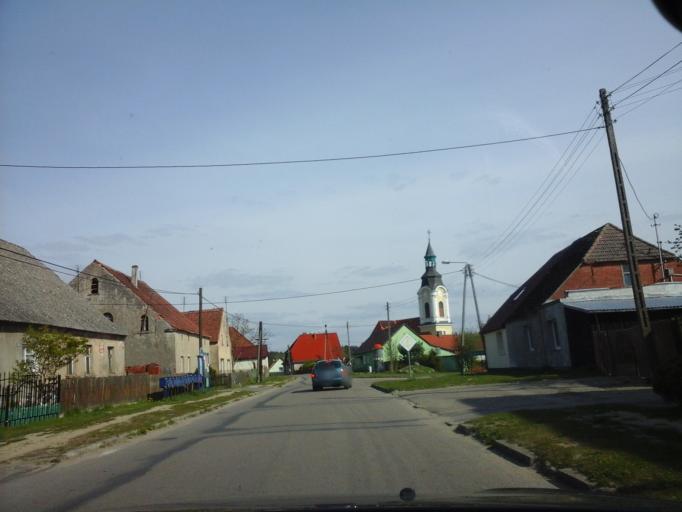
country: PL
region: West Pomeranian Voivodeship
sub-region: Powiat choszczenski
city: Krzecin
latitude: 53.0404
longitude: 15.5361
